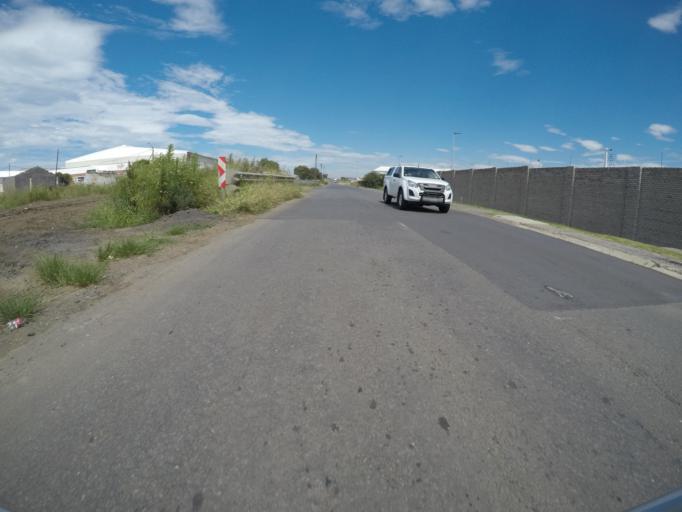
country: ZA
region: Eastern Cape
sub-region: Buffalo City Metropolitan Municipality
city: East London
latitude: -33.0338
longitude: 27.8901
